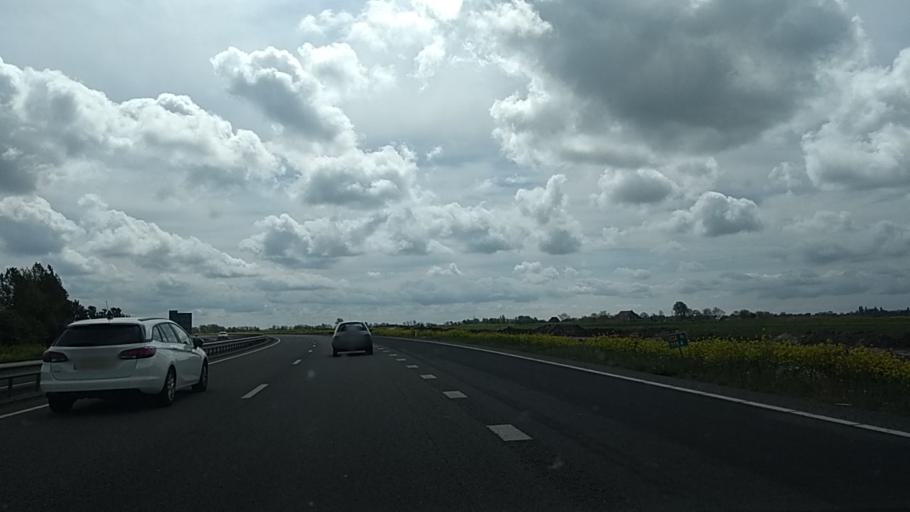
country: NL
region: Friesland
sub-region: Sudwest Fryslan
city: IJlst
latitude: 53.0308
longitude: 5.6239
